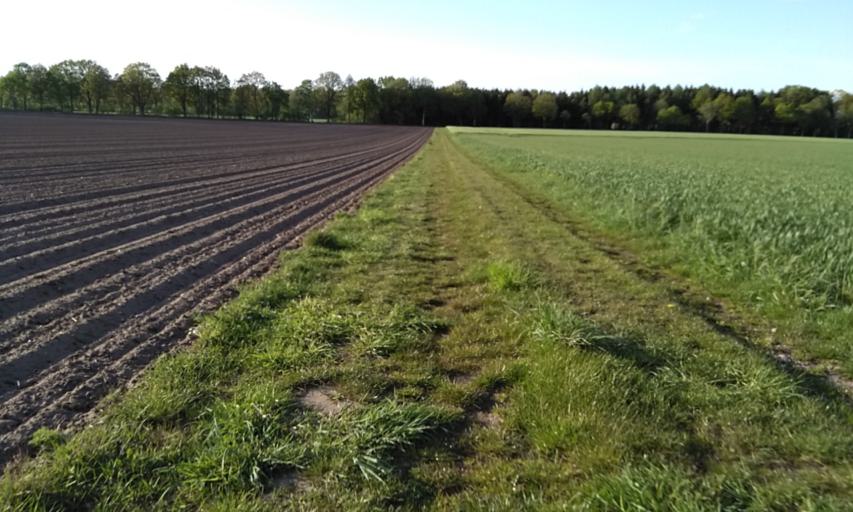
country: DE
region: Lower Saxony
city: Sauensiek
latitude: 53.4058
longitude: 9.5866
